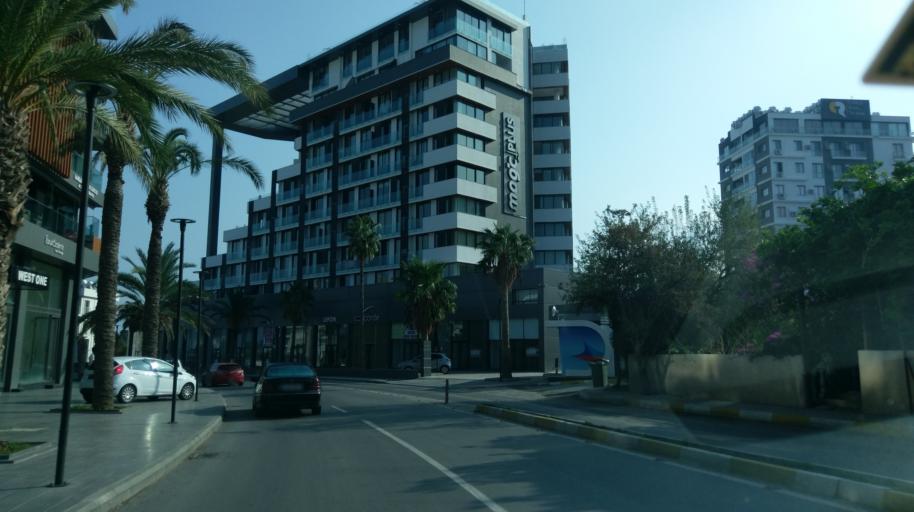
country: CY
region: Keryneia
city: Kyrenia
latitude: 35.3294
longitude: 33.3289
